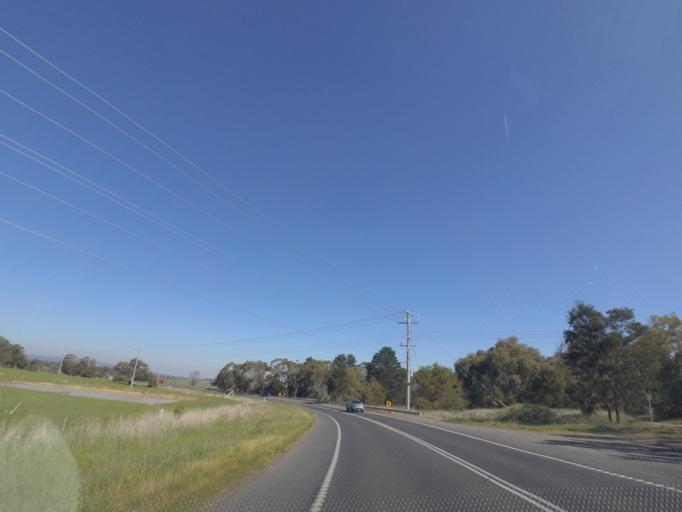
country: AU
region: Victoria
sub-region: Whittlesea
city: Whittlesea
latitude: -37.3367
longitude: 144.9828
